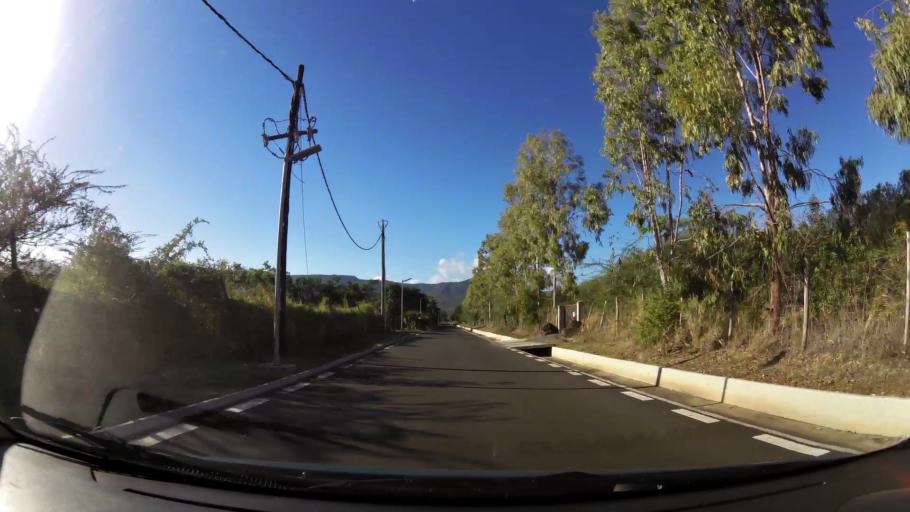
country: MU
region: Black River
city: Tamarin
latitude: -20.3416
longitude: 57.3888
